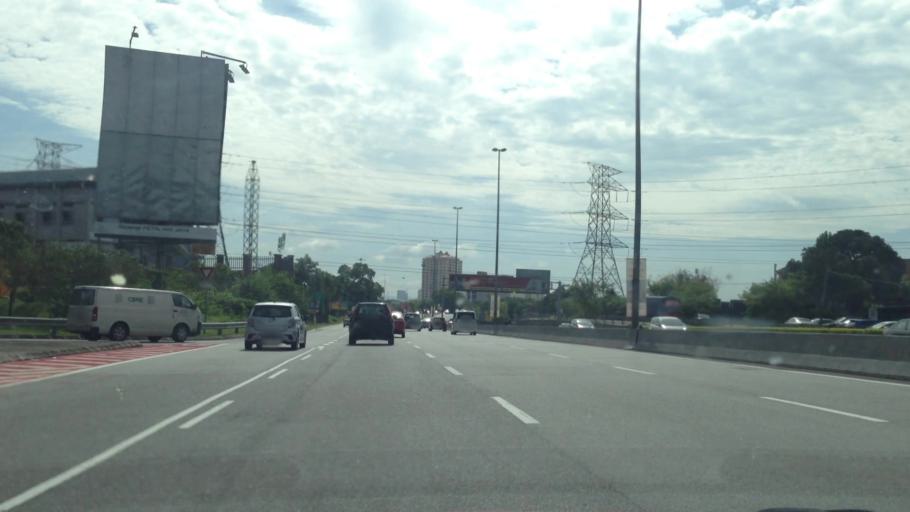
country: MY
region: Selangor
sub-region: Petaling
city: Petaling Jaya
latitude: 3.0755
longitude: 101.6185
